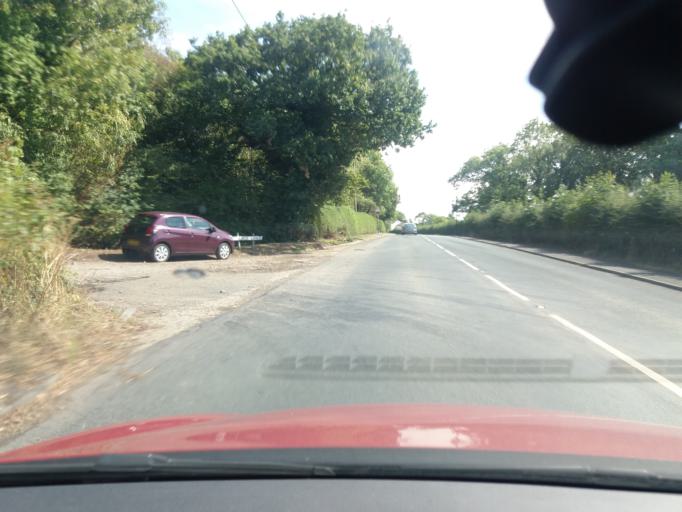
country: GB
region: England
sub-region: Lancashire
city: Euxton
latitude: 53.6611
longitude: -2.7043
